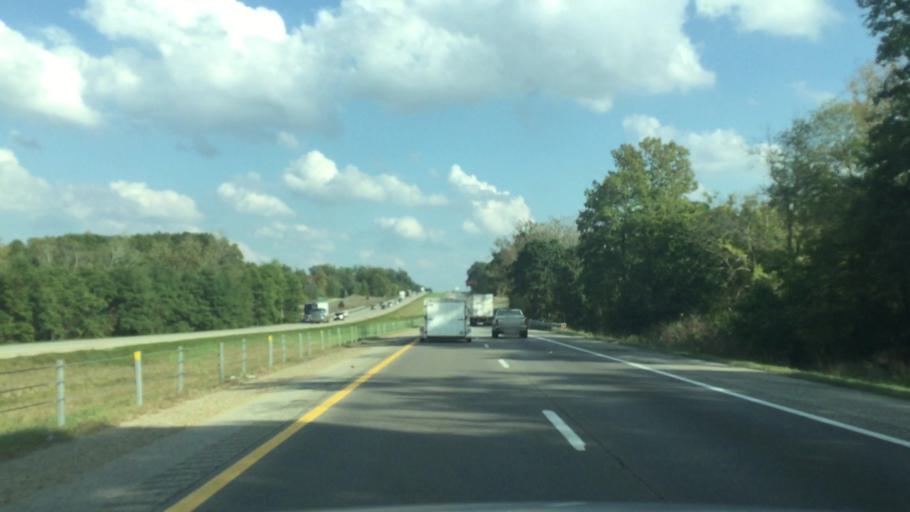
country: US
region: Michigan
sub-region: Kalamazoo County
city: Galesburg
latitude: 42.2796
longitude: -85.3337
